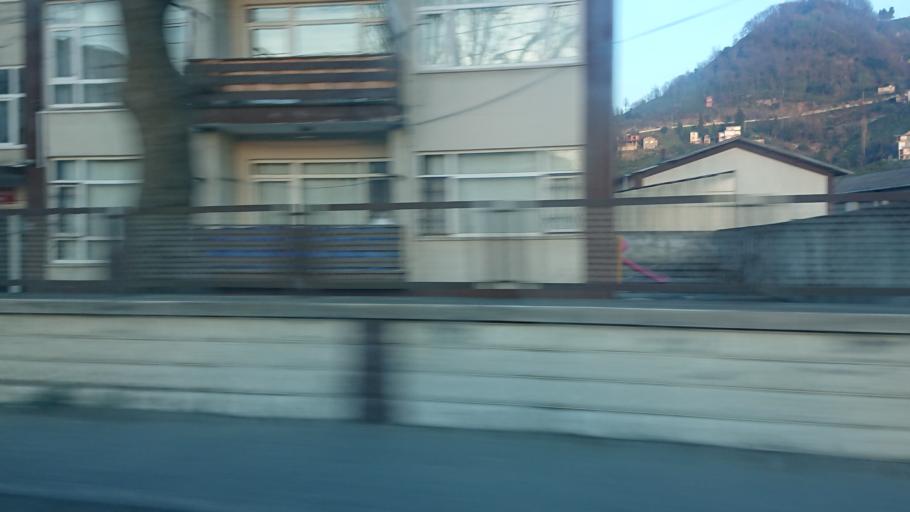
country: TR
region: Rize
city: Gundogdu
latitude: 41.0409
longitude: 40.5793
